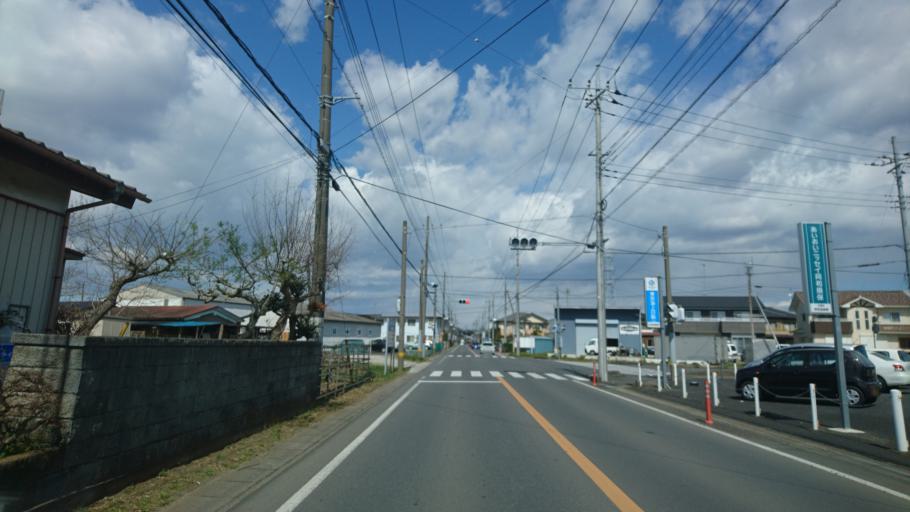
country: JP
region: Ibaraki
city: Ishige
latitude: 36.1970
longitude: 139.9522
